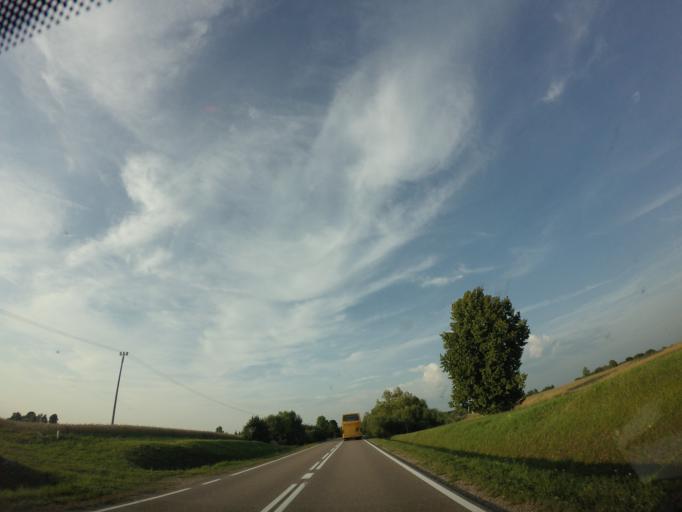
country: PL
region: Podlasie
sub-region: Powiat sejnenski
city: Sejny
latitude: 54.0852
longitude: 23.3816
